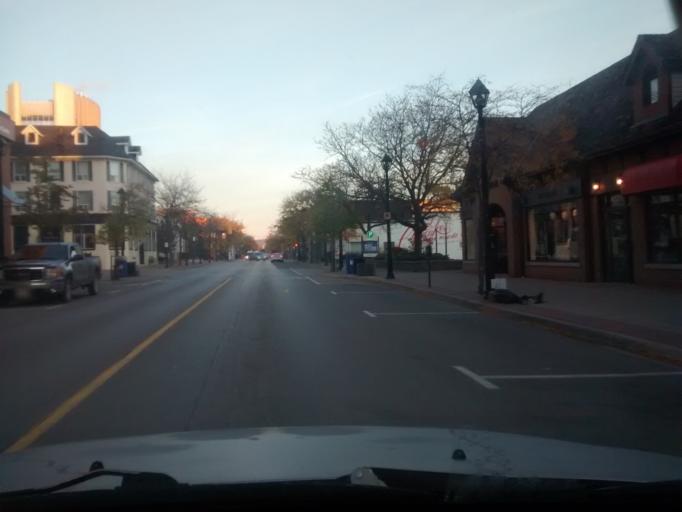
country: CA
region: Ontario
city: Burlington
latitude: 43.3252
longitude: -79.7972
